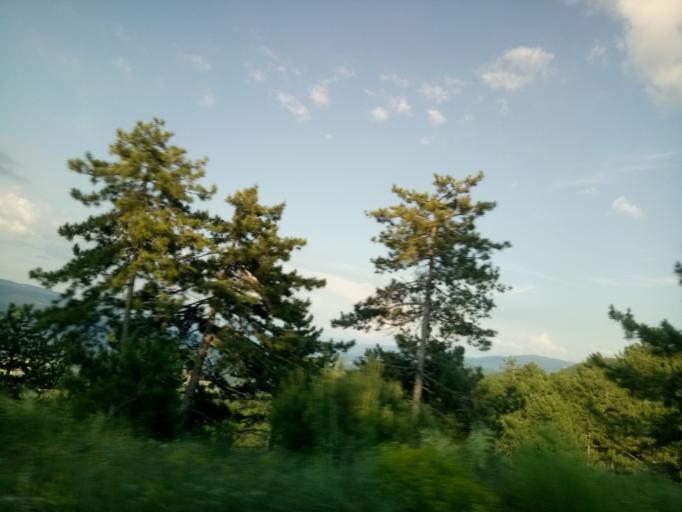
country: TR
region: Karabuk
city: Karabuk
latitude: 41.1191
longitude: 32.6069
